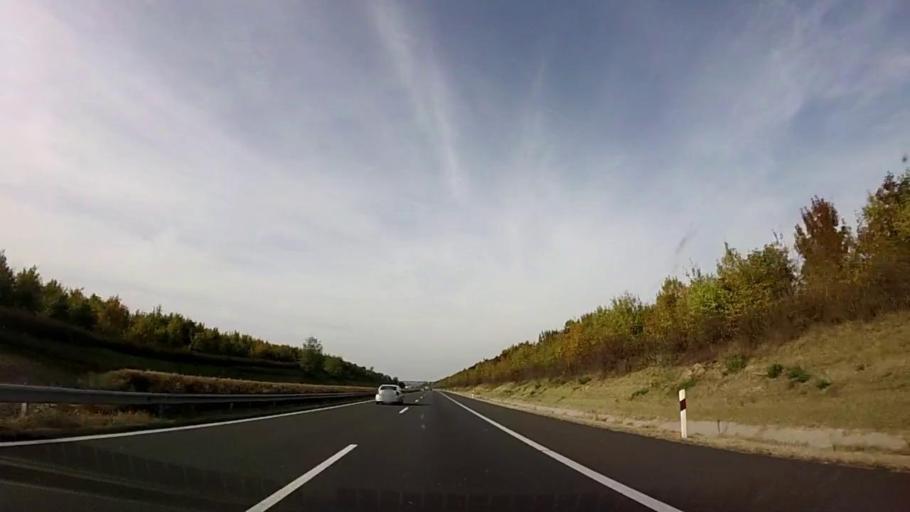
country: HU
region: Somogy
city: Balatonszarszo
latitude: 46.8099
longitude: 17.8348
